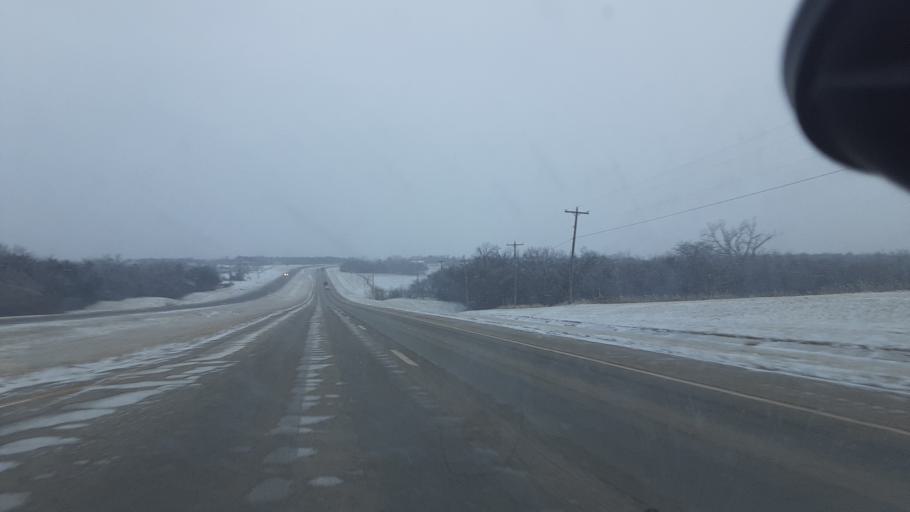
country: US
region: Oklahoma
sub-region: Logan County
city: Guthrie
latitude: 35.8917
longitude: -97.3638
